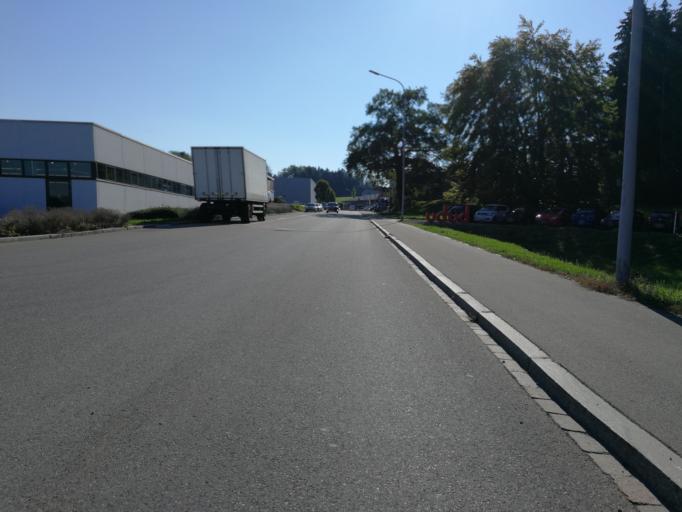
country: CH
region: Zurich
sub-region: Bezirk Uster
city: Moenchaltorf / Dorf
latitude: 47.3038
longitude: 8.7187
